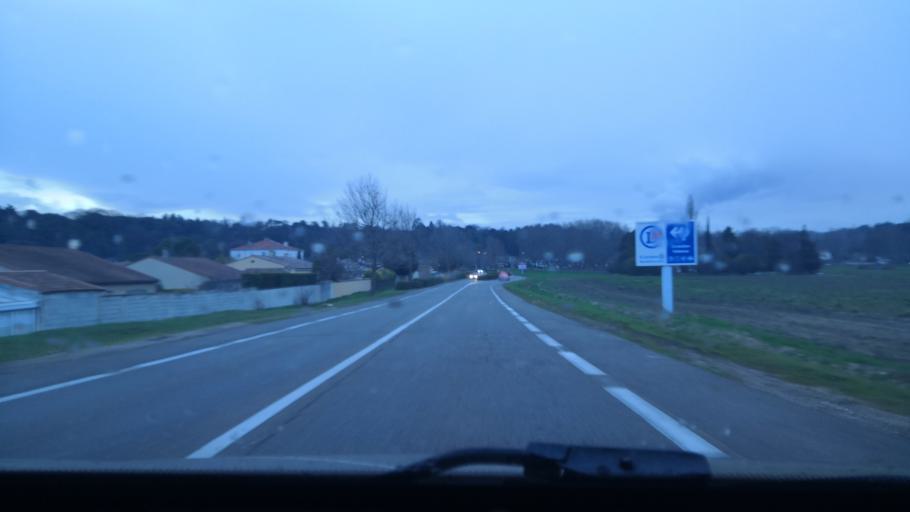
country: FR
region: Rhone-Alpes
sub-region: Departement de la Drome
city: Montelimar
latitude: 44.5584
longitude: 4.7630
